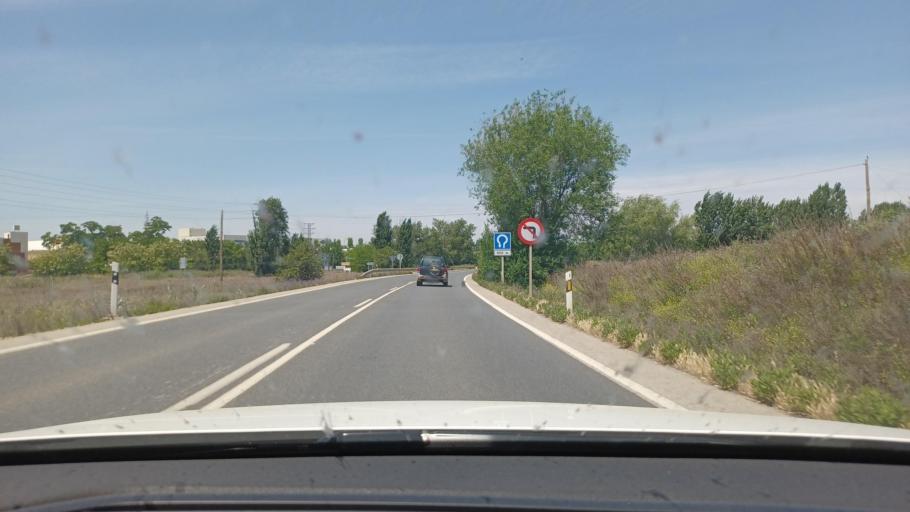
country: ES
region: Madrid
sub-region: Provincia de Madrid
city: Meco
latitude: 40.5373
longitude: -3.3002
